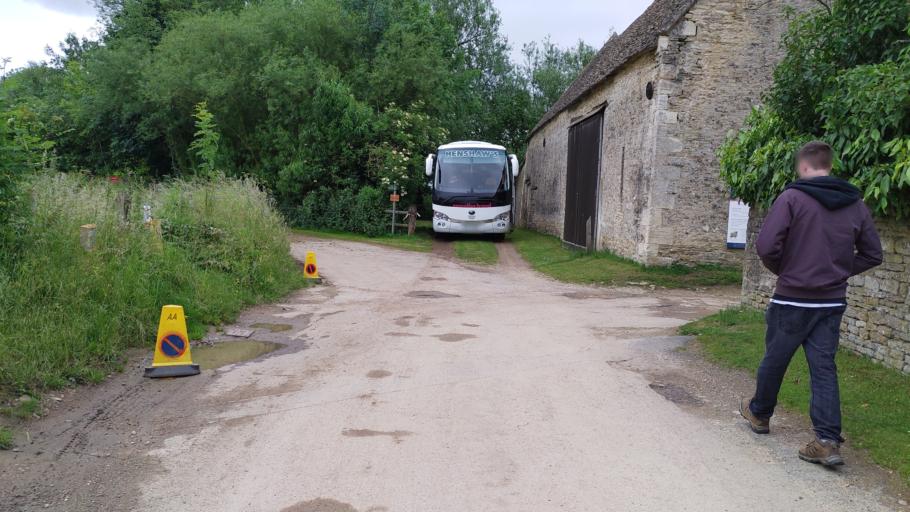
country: GB
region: England
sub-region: Gloucestershire
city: Lechlade
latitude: 51.6883
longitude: -1.6379
